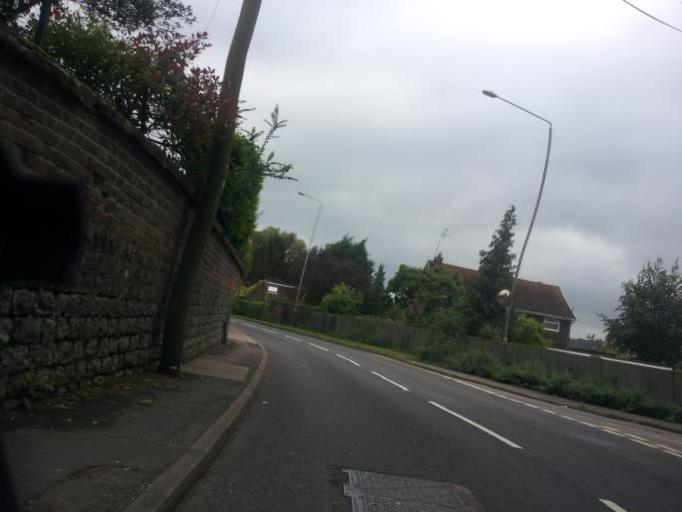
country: GB
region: England
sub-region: Kent
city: Wateringbury
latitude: 51.2566
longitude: 0.4182
